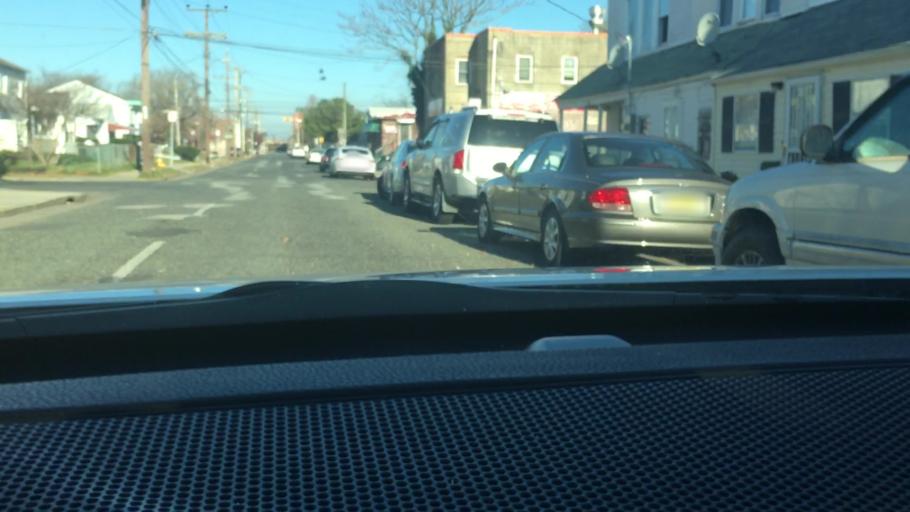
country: US
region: New Jersey
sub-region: Atlantic County
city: Atlantic City
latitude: 39.3688
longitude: -74.4341
